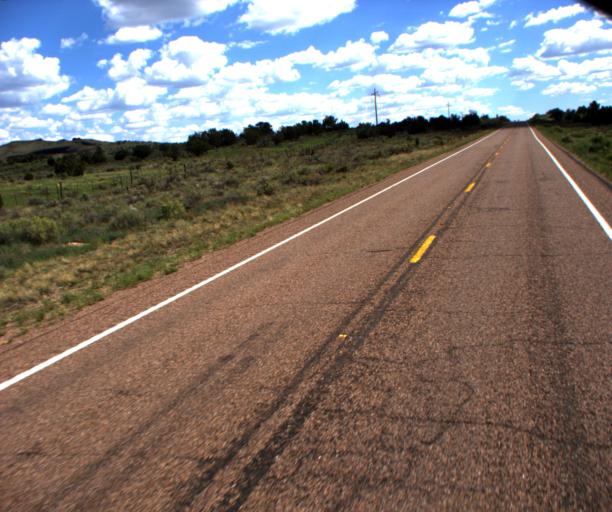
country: US
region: Arizona
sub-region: Coconino County
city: Williams
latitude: 35.5592
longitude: -112.1581
